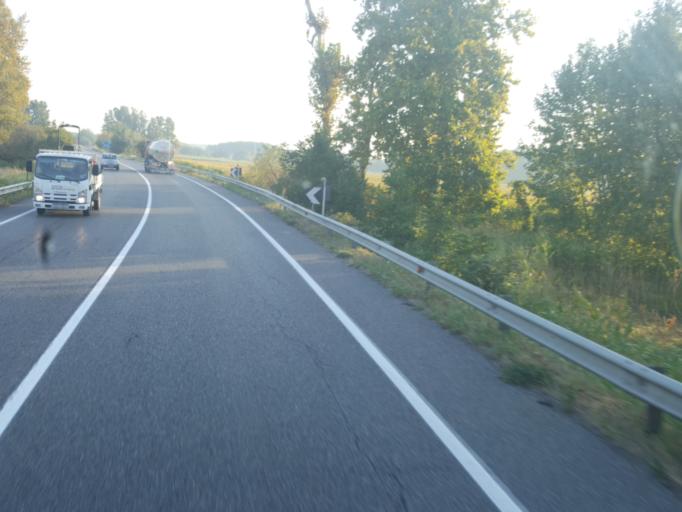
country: IT
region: Lombardy
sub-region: Provincia di Cremona
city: Ripalta Nuova
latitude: 45.3467
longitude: 9.7038
